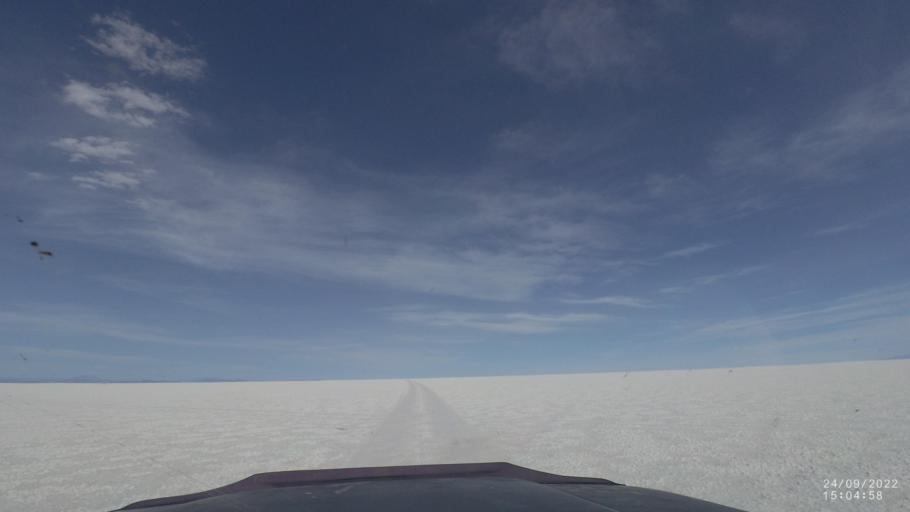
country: BO
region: Potosi
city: Colchani
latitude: -19.9031
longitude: -67.5207
